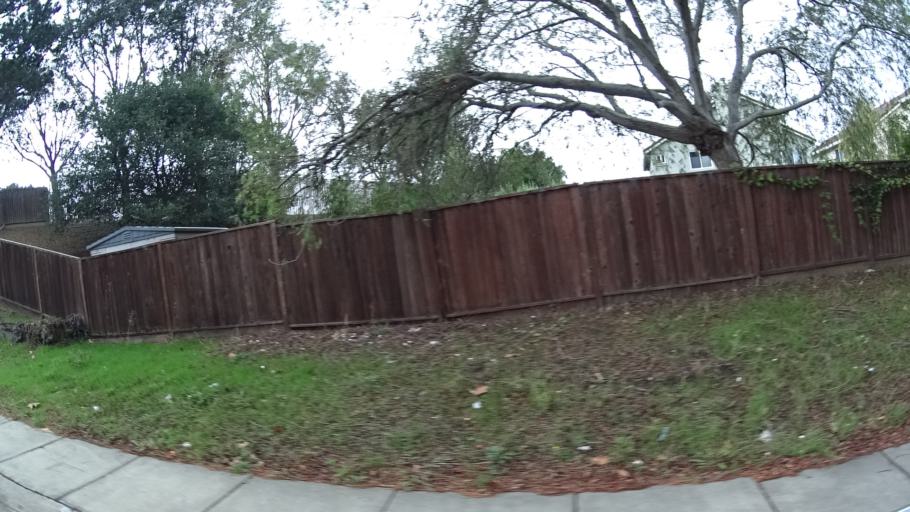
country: US
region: California
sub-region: San Mateo County
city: San Bruno
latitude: 37.6418
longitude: -122.4341
